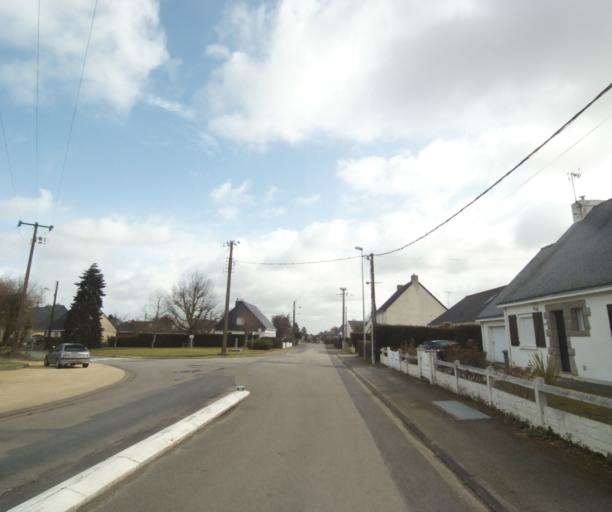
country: FR
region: Pays de la Loire
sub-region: Departement de la Loire-Atlantique
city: Bouvron
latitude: 47.4154
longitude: -1.8536
